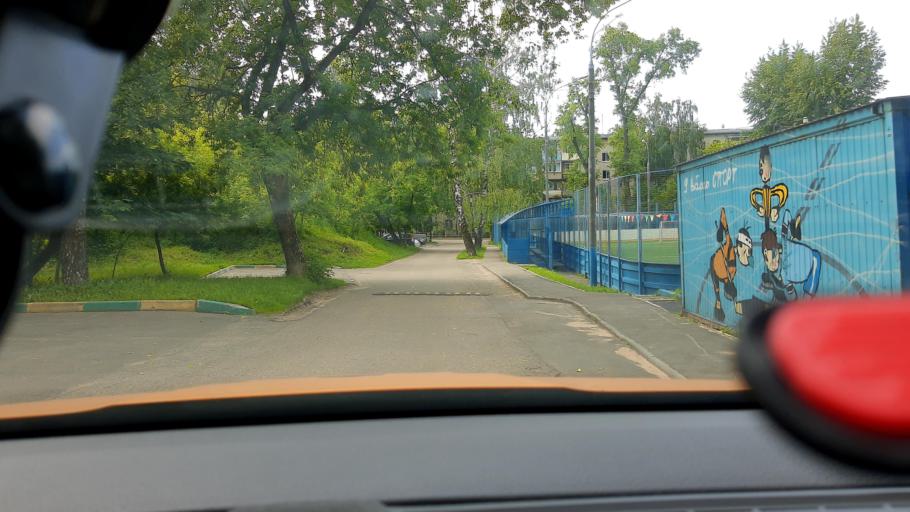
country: RU
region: Moscow
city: Zhulebino
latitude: 55.7193
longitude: 37.8645
